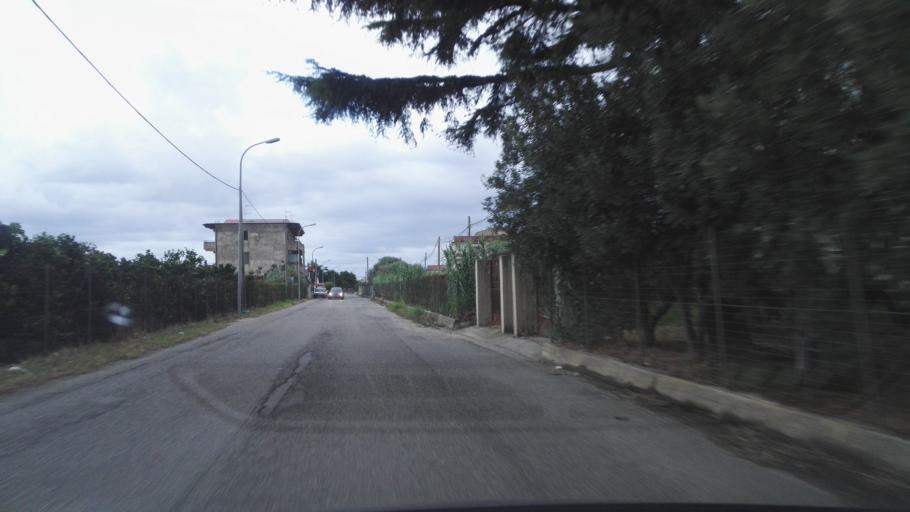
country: IT
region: Calabria
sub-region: Provincia di Reggio Calabria
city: Caulonia Marina
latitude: 38.3580
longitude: 16.4697
